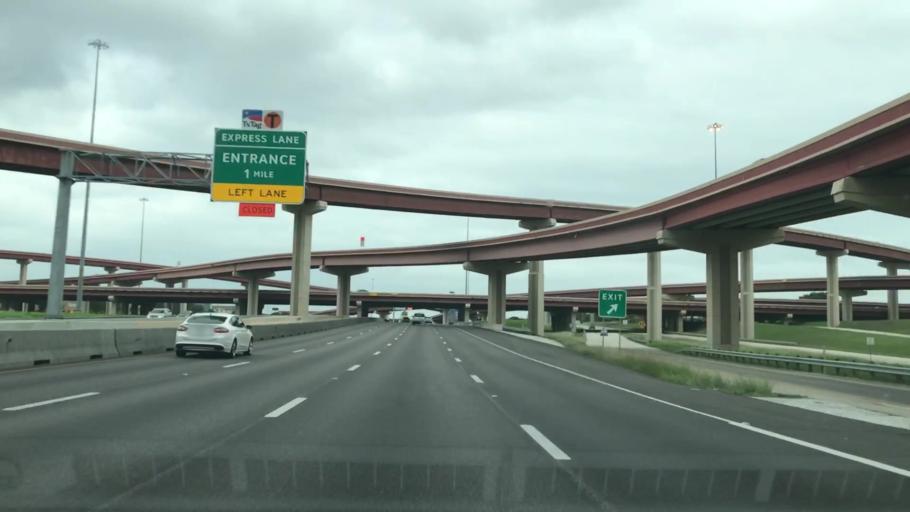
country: US
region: Texas
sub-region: Tarrant County
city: Euless
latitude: 32.8369
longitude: -97.0195
